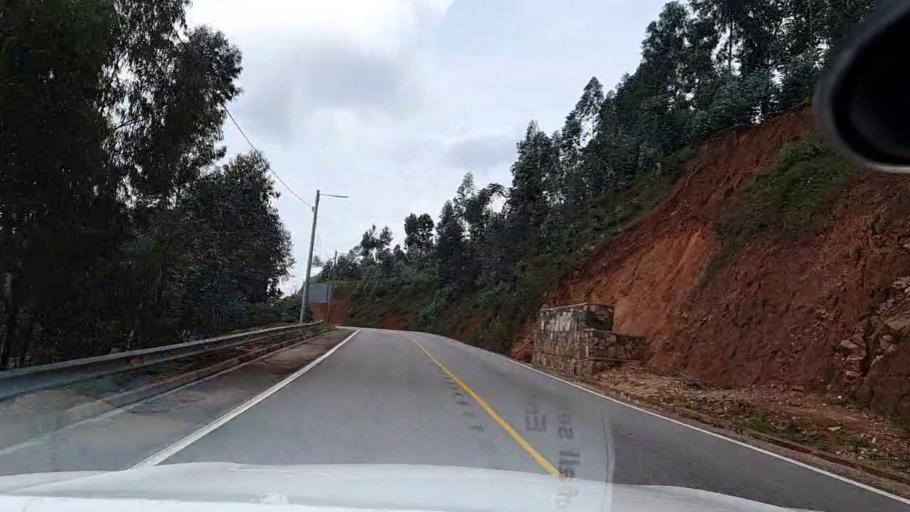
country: RW
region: Southern Province
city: Nzega
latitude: -2.5131
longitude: 29.4637
